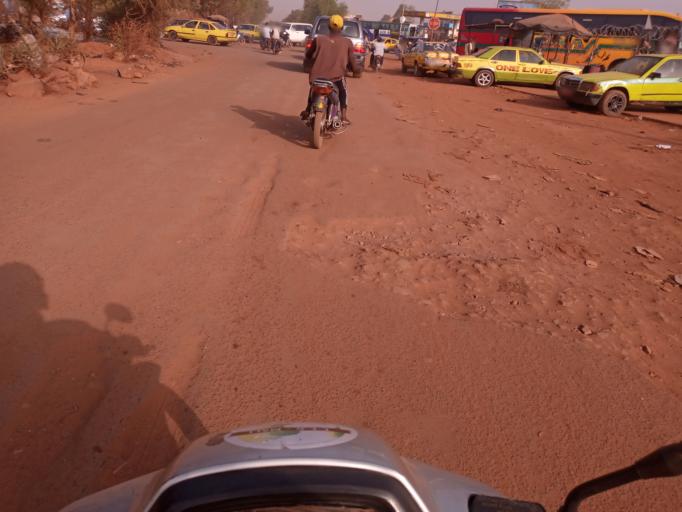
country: ML
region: Bamako
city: Bamako
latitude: 12.5928
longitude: -7.9536
